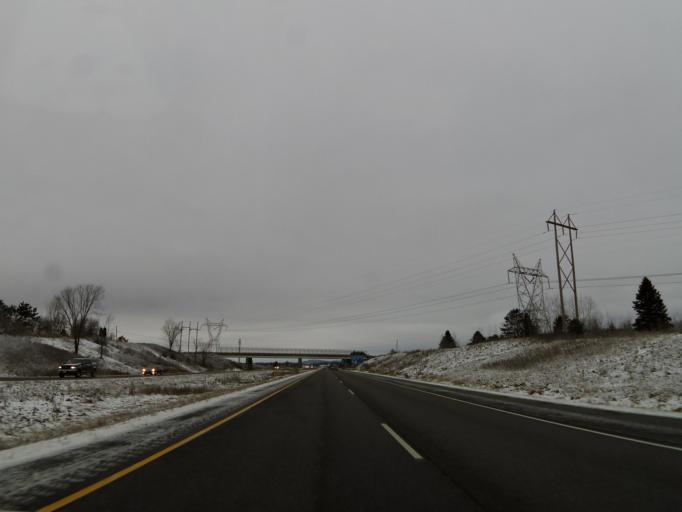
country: US
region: Wisconsin
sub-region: Eau Claire County
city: Eau Claire
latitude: 44.8357
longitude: -91.5869
